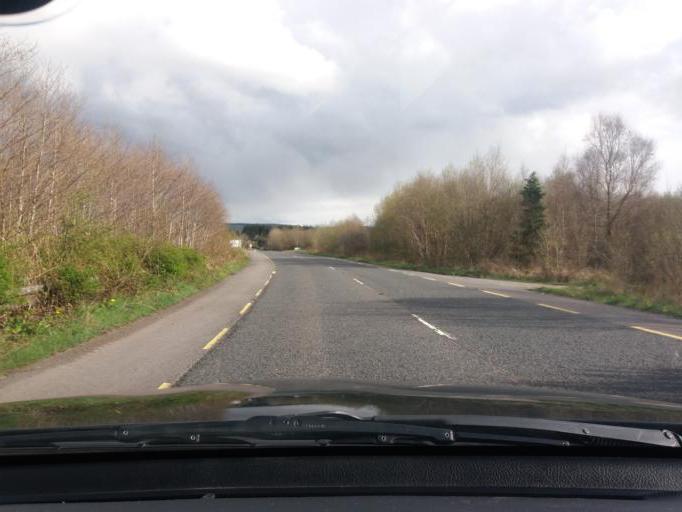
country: IE
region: Connaught
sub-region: County Leitrim
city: Manorhamilton
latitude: 54.3230
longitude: -8.2054
